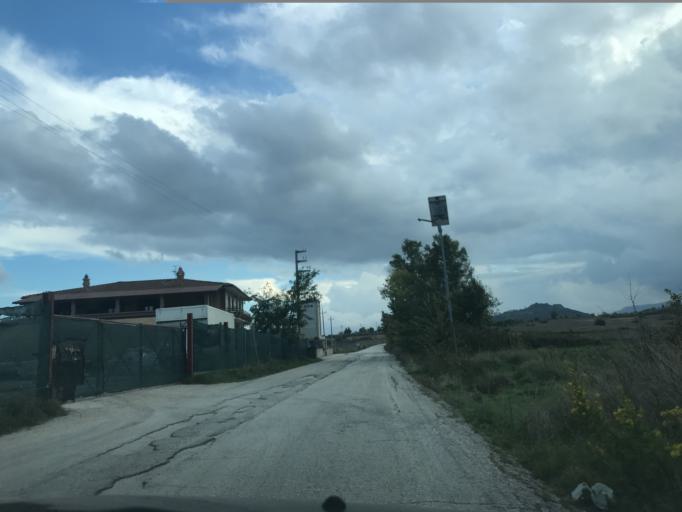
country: IT
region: Molise
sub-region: Provincia di Isernia
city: Bagnoli del Trigno
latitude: 41.6951
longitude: 14.4616
